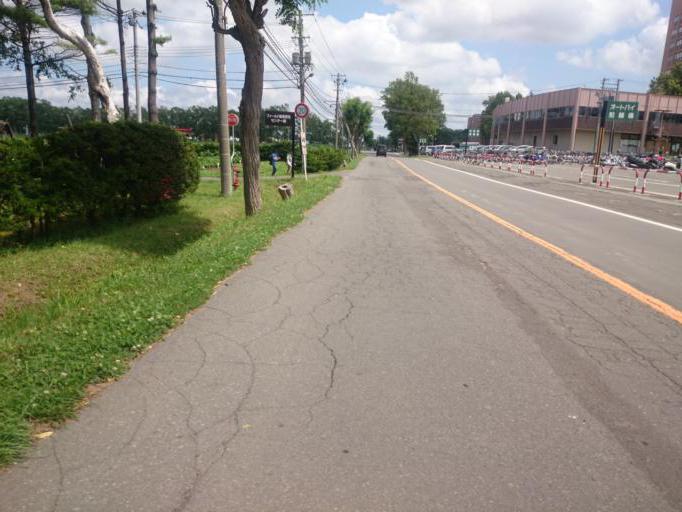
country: JP
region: Hokkaido
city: Ebetsu
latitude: 43.0729
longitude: 141.5070
